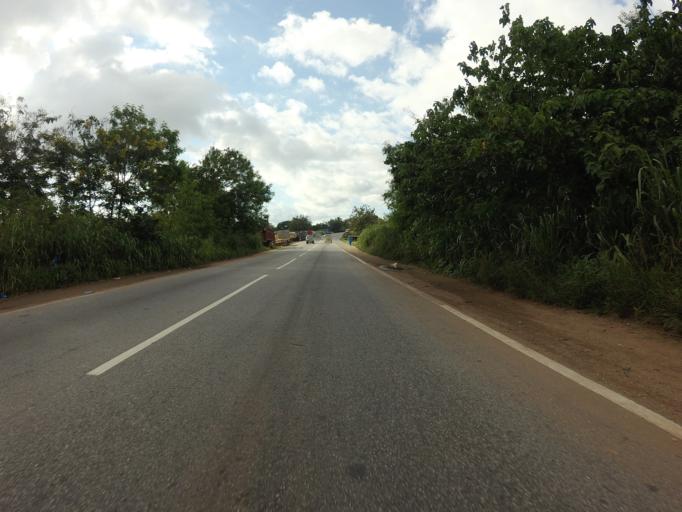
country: GH
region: Ashanti
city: Tafo
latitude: 6.8315
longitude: -1.6498
